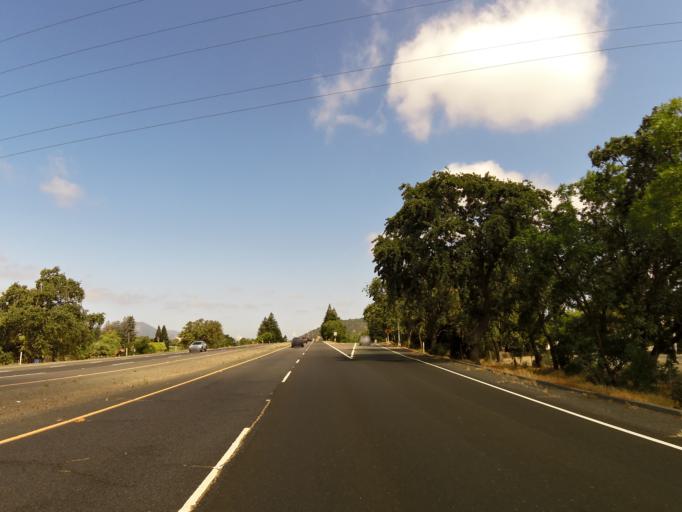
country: US
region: California
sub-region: Napa County
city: Yountville
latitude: 38.3955
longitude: -122.3566
